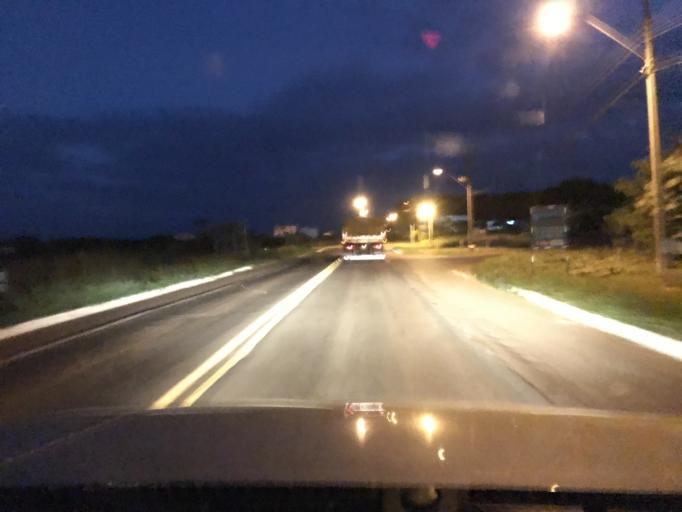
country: PY
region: Canindeyu
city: Salto del Guaira
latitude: -24.1044
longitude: -54.2390
